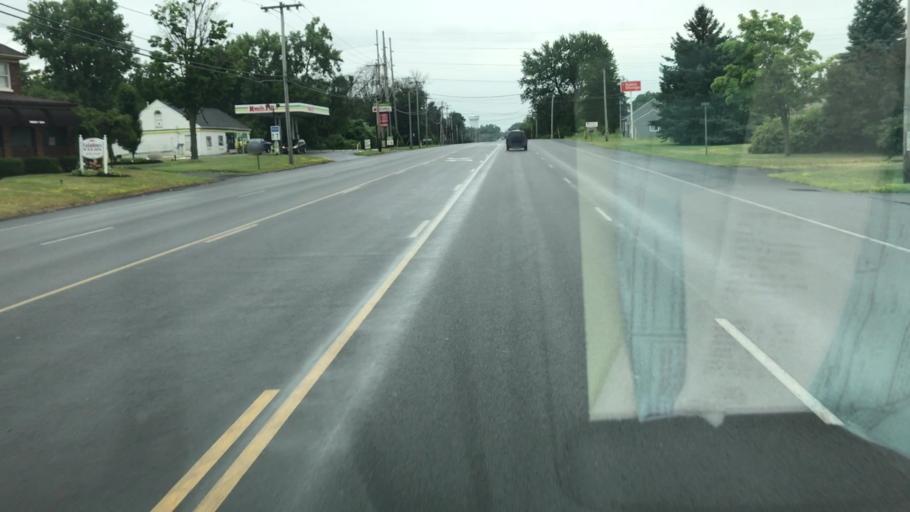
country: US
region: New York
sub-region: Onondaga County
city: Liverpool
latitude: 43.1271
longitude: -76.2183
